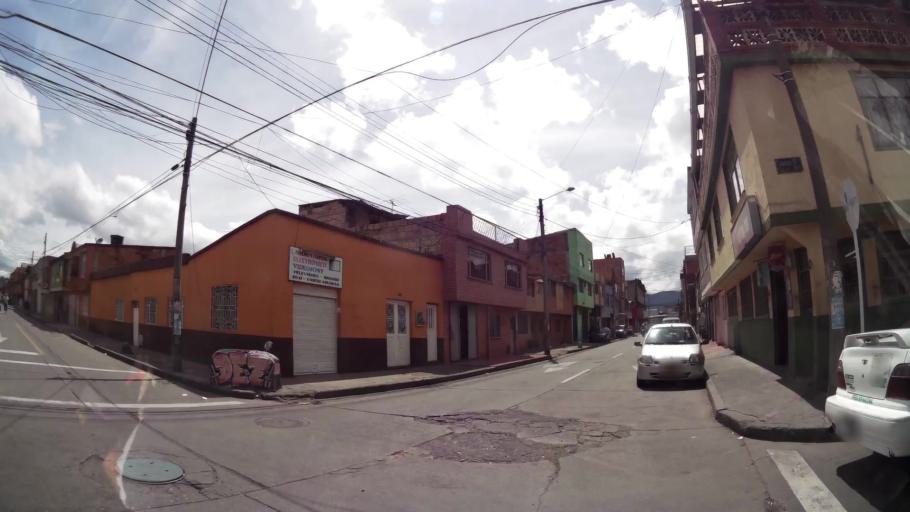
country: CO
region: Bogota D.C.
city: Bogota
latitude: 4.6918
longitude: -74.1094
